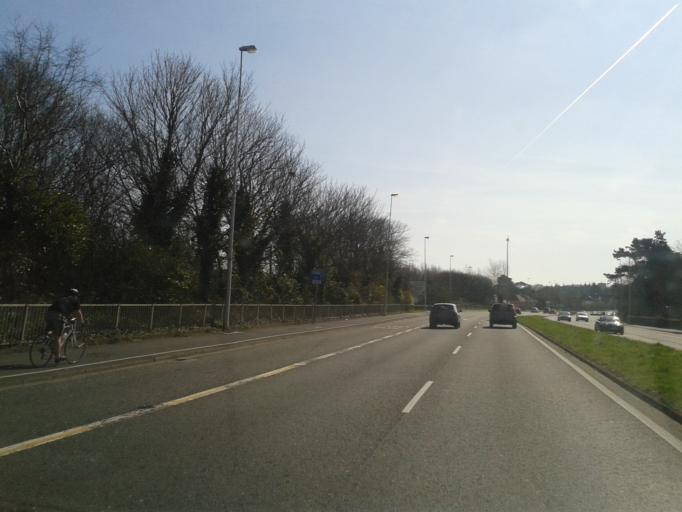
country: IE
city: Booterstown
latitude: 53.2910
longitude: -6.1978
